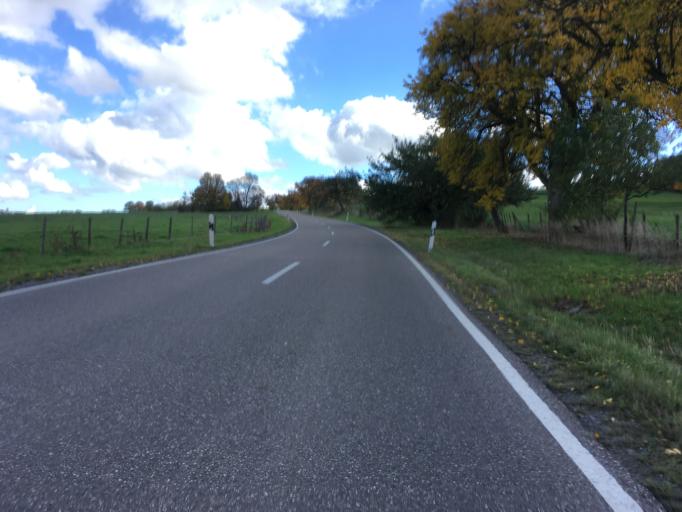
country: DE
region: Baden-Wuerttemberg
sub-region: Regierungsbezirk Stuttgart
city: Waldenburg
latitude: 49.2002
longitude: 9.6419
